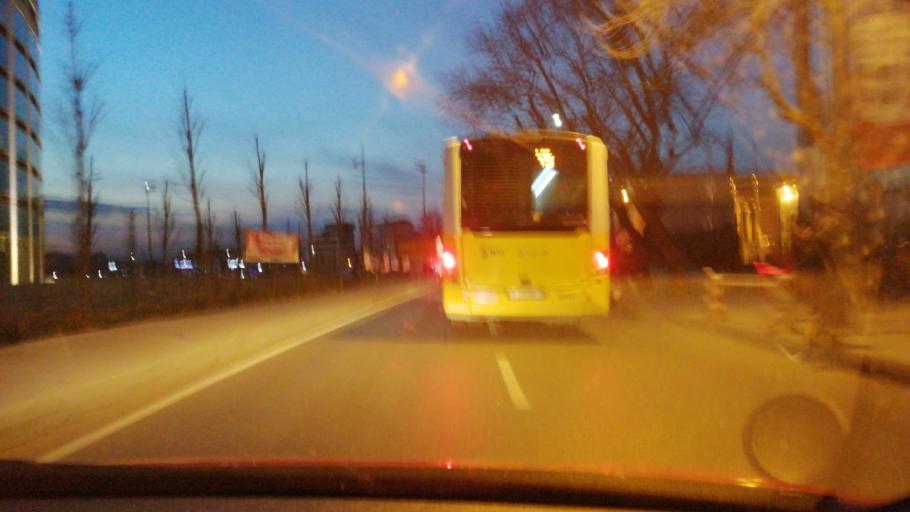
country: TR
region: Istanbul
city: Sisli
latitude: 41.0697
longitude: 28.9821
